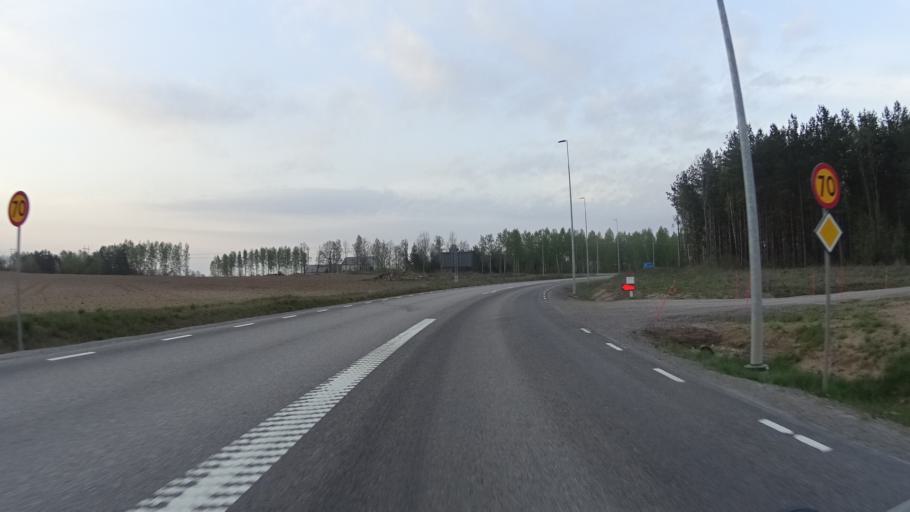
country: SE
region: Vaestra Goetaland
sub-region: Gotene Kommun
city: Kallby
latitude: 58.4995
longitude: 13.3049
